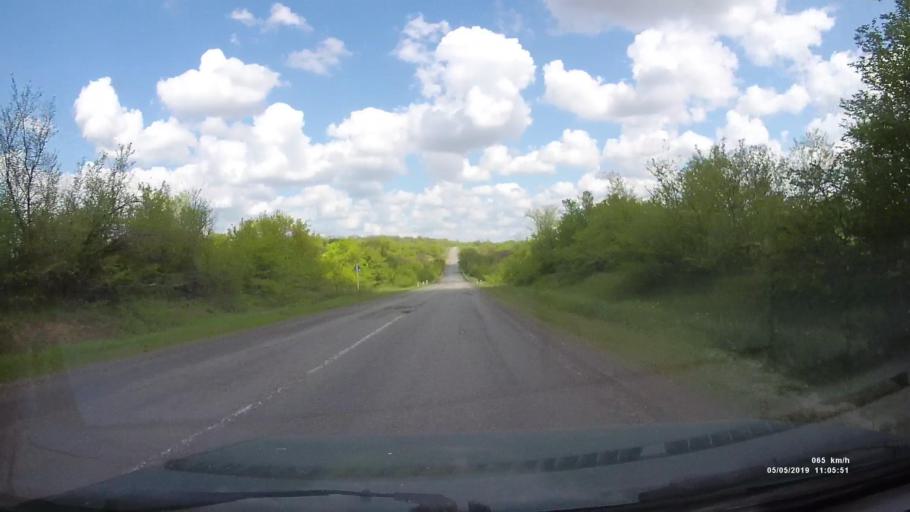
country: RU
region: Rostov
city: Ust'-Donetskiy
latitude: 47.7099
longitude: 40.9113
